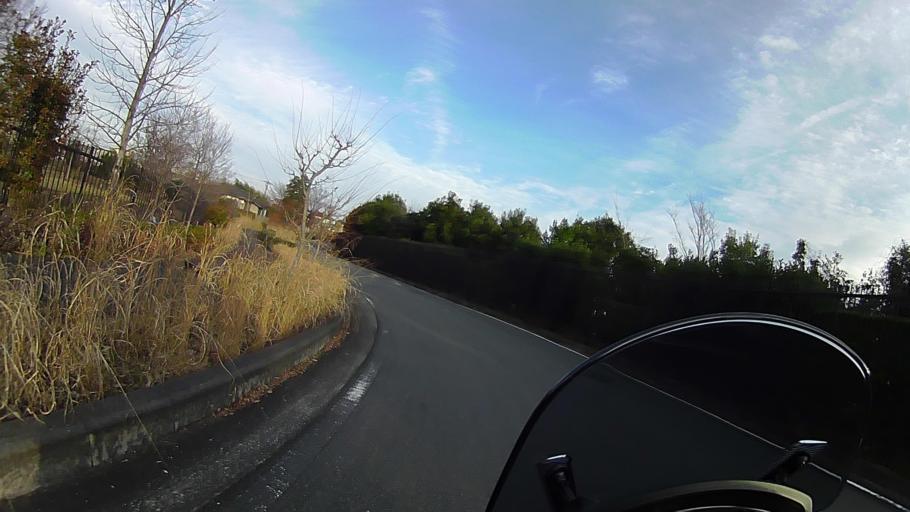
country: JP
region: Kanagawa
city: Atsugi
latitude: 35.4240
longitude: 139.4180
